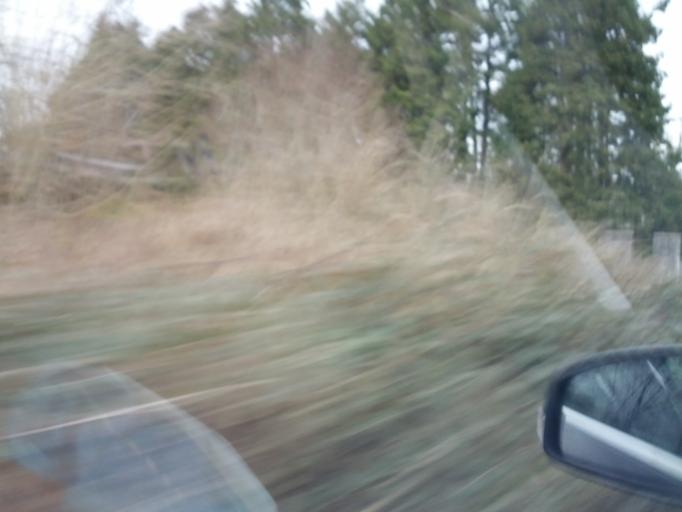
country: IE
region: Connaught
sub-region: County Galway
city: Oranmore
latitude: 53.2558
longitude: -8.8365
